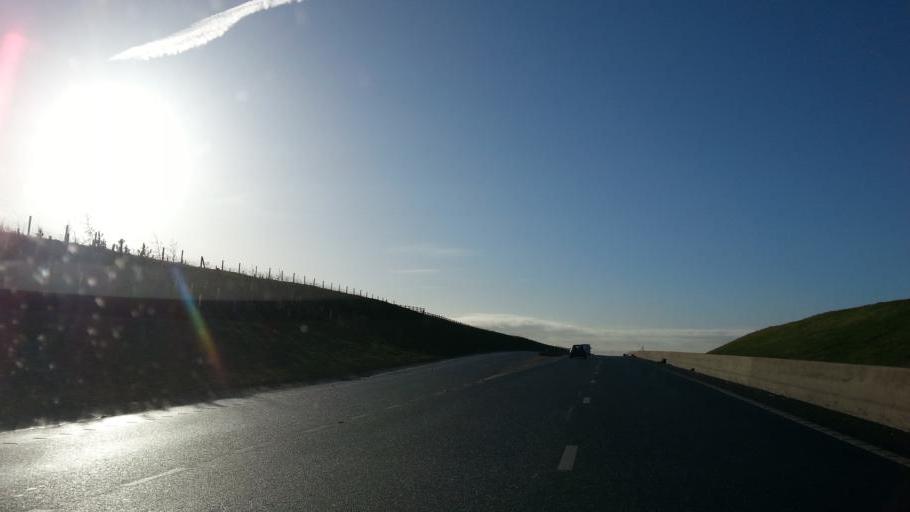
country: GB
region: England
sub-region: Nottinghamshire
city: Gotham
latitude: 52.8704
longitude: -1.2363
